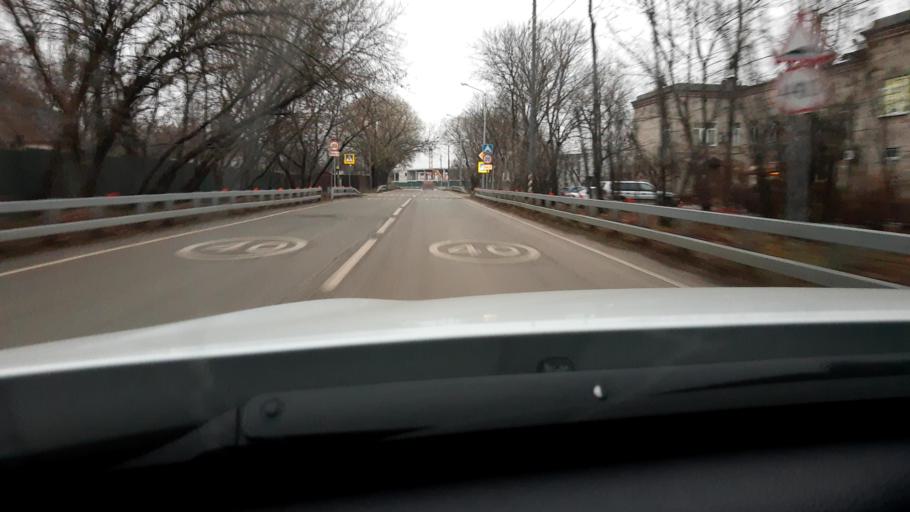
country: RU
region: Moscow
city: Zhulebino
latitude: 55.7164
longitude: 37.8475
